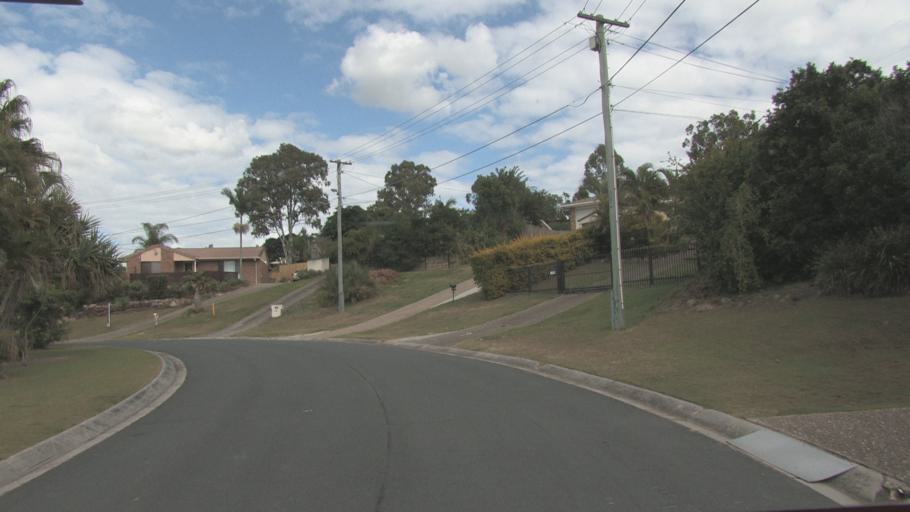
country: AU
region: Queensland
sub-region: Logan
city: Windaroo
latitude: -27.7297
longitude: 153.2048
